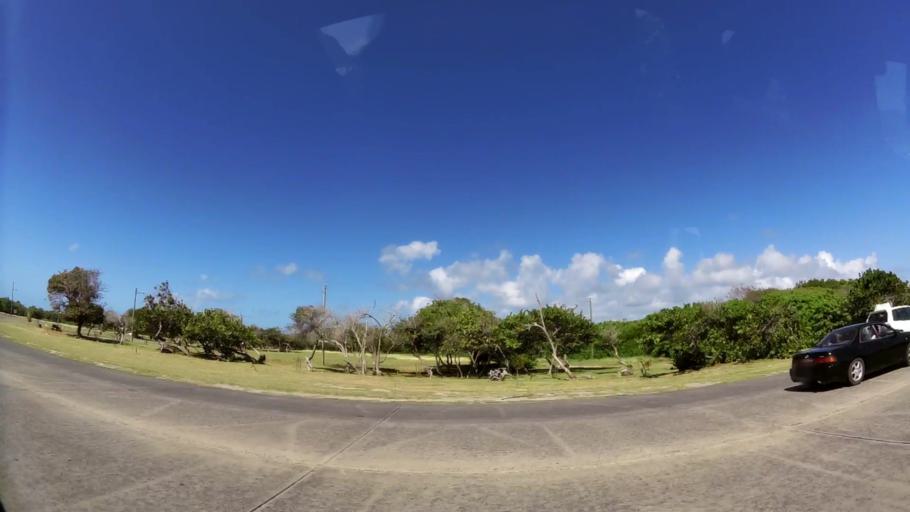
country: LC
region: Vieux-Fort
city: Vieux Fort
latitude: 13.7285
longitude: -60.9449
